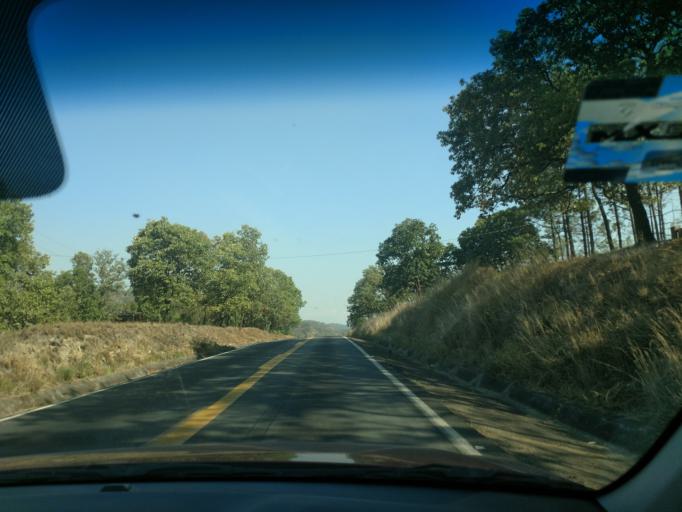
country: MX
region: Nayarit
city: Santa Maria del Oro
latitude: 21.2716
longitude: -104.6479
